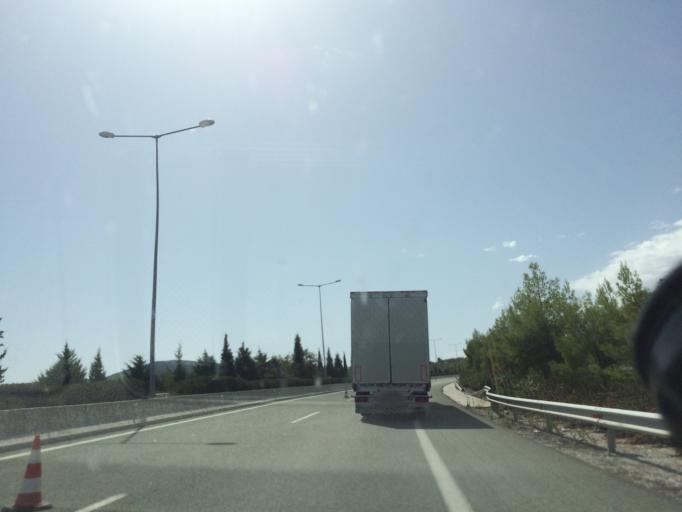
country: GR
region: Thessaly
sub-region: Nomos Magnisias
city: Pteleos
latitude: 39.0101
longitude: 22.9132
